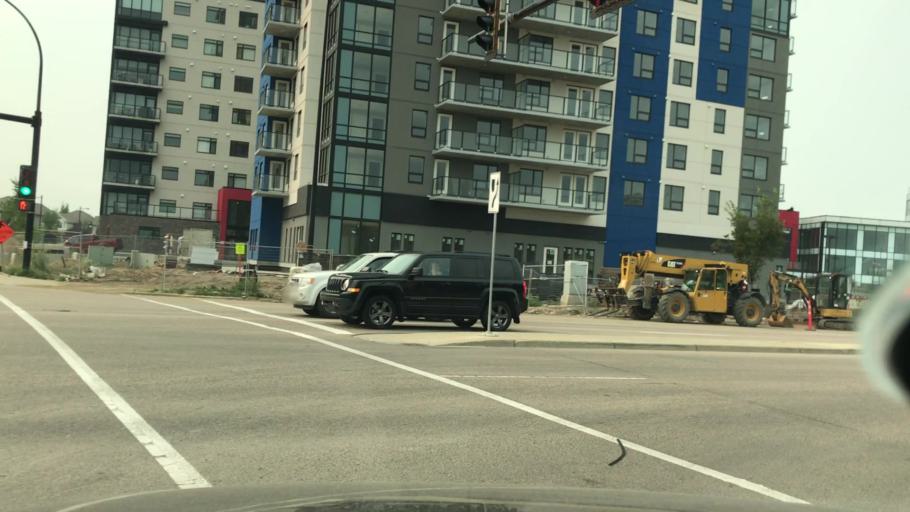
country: CA
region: Alberta
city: Devon
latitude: 53.4346
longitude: -113.5991
